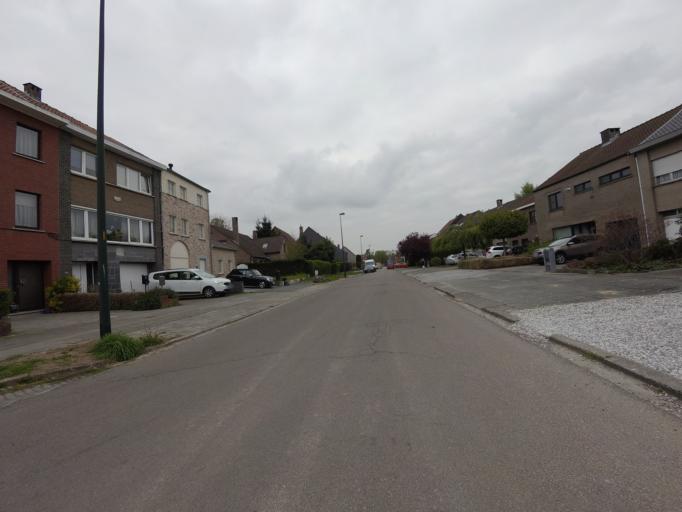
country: BE
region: Flanders
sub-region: Provincie Vlaams-Brabant
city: Grimbergen
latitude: 50.9115
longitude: 4.3794
